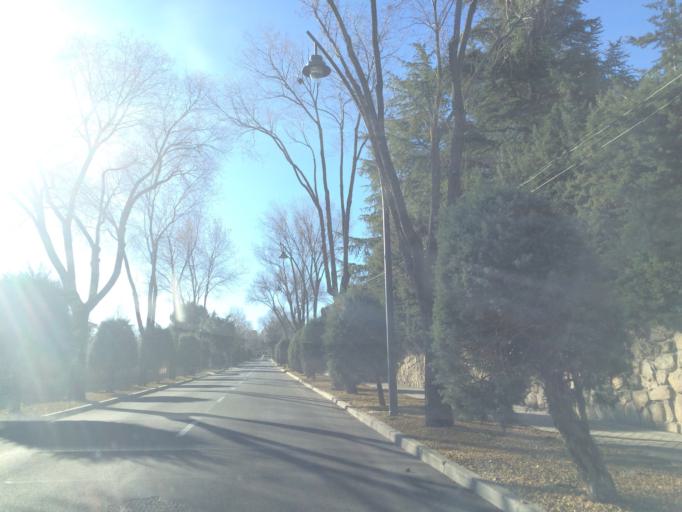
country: ES
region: Madrid
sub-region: Provincia de Madrid
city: Tres Cantos
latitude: 40.6110
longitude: -3.6890
